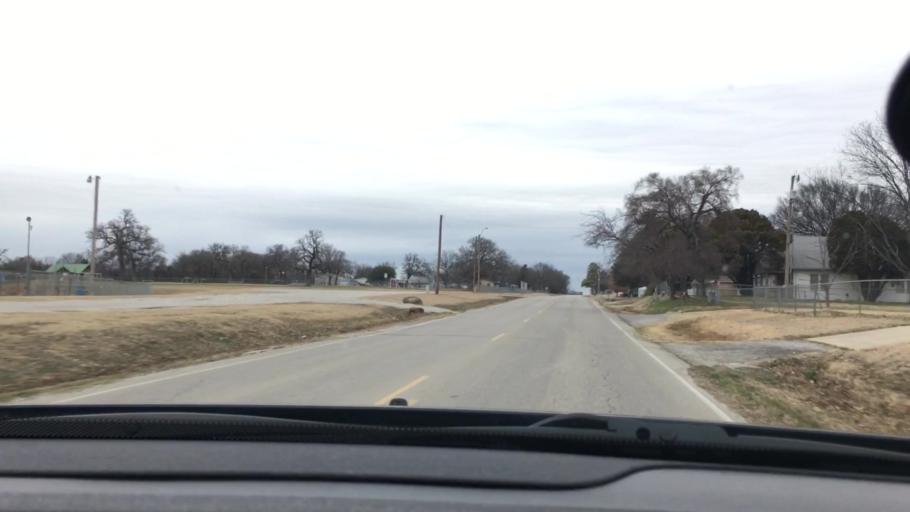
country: US
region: Oklahoma
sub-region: Carter County
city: Ardmore
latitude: 34.1700
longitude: -97.1080
